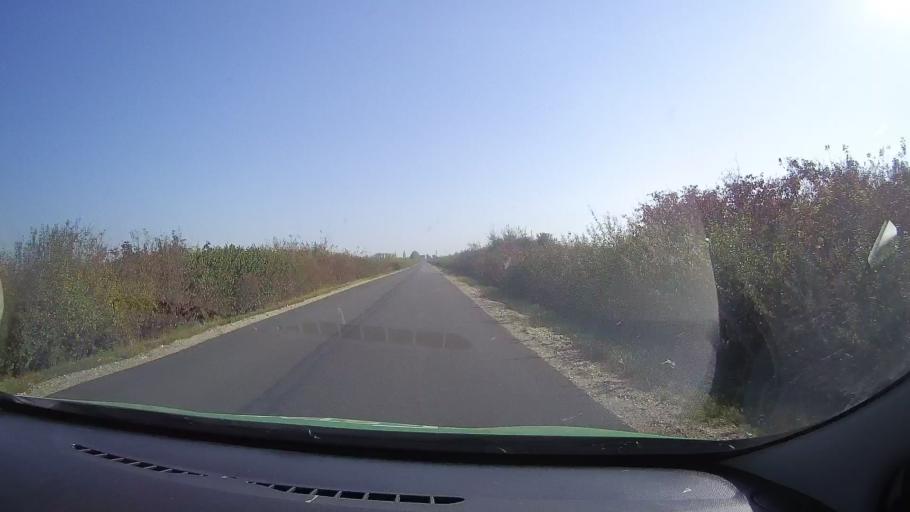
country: RO
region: Satu Mare
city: Carei
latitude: 47.6929
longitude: 22.4304
